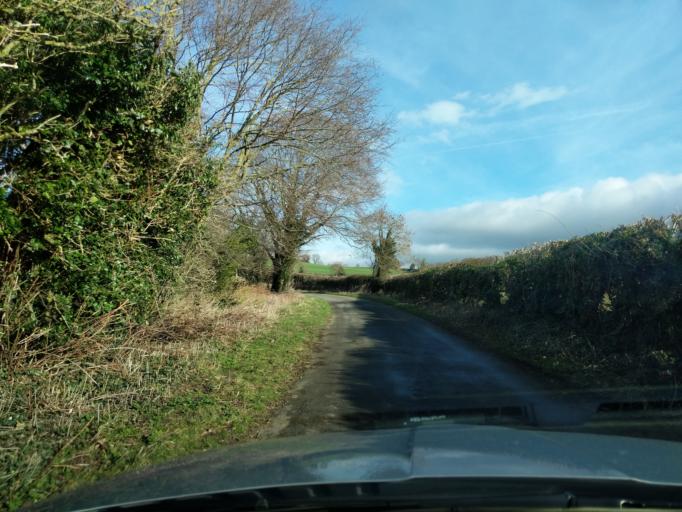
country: GB
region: England
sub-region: North Yorkshire
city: Catterick Garrison
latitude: 54.3379
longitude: -1.6947
